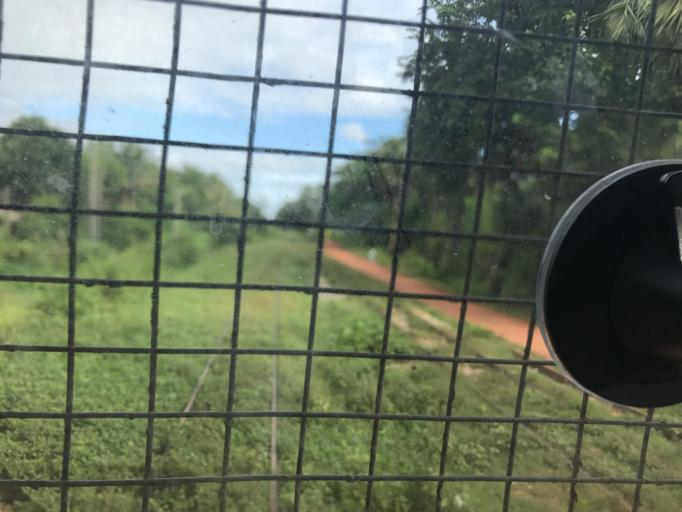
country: MM
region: Bago
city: Letpandan
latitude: 17.8949
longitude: 95.7247
